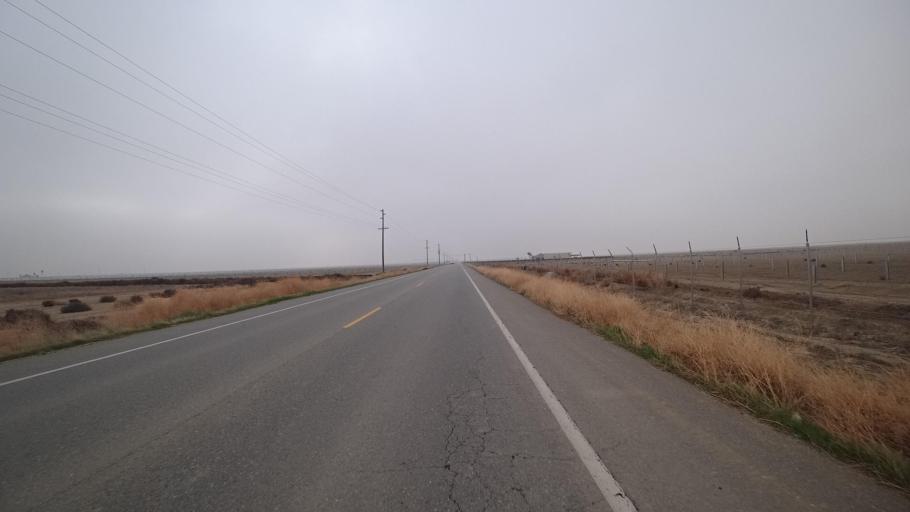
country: US
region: California
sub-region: Kern County
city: Greenfield
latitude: 35.1223
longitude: -119.1098
